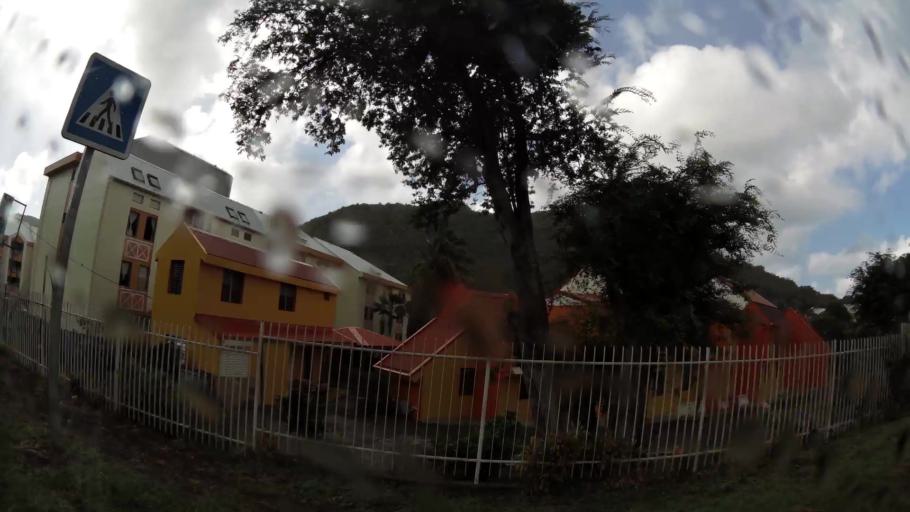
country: MQ
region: Martinique
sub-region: Martinique
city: Les Trois-Ilets
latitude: 14.4982
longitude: -61.0794
